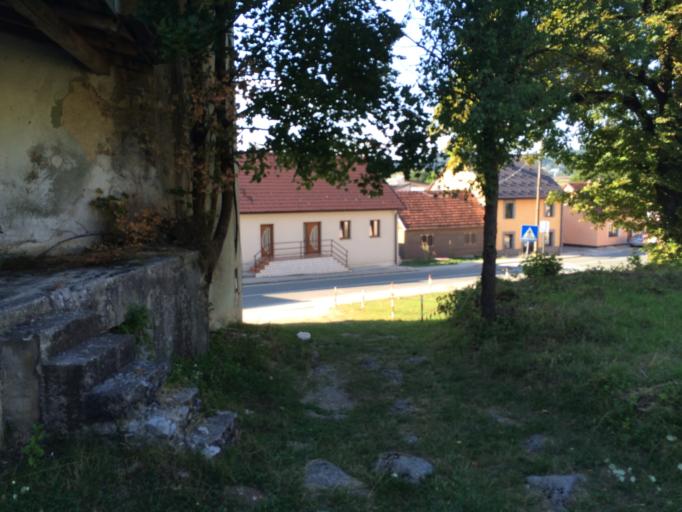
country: HR
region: Licko-Senjska
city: Brinje
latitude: 44.9990
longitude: 15.1306
